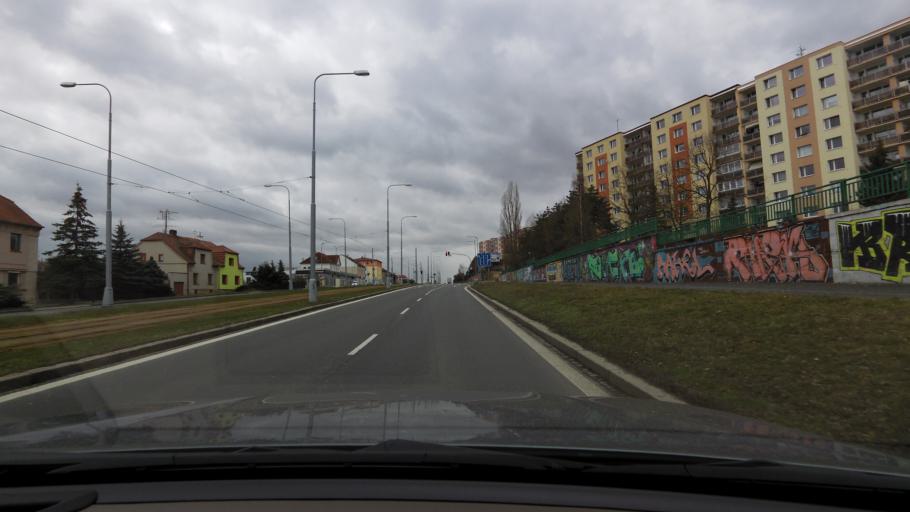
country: CZ
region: Plzensky
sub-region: Okres Plzen-Mesto
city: Pilsen
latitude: 49.7726
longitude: 13.3776
